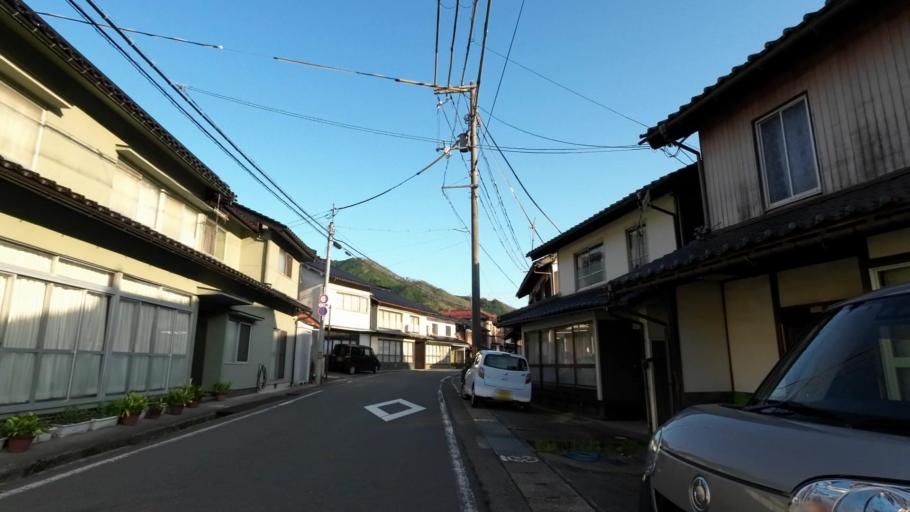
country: JP
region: Hyogo
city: Toyooka
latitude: 35.3834
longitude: 134.8135
